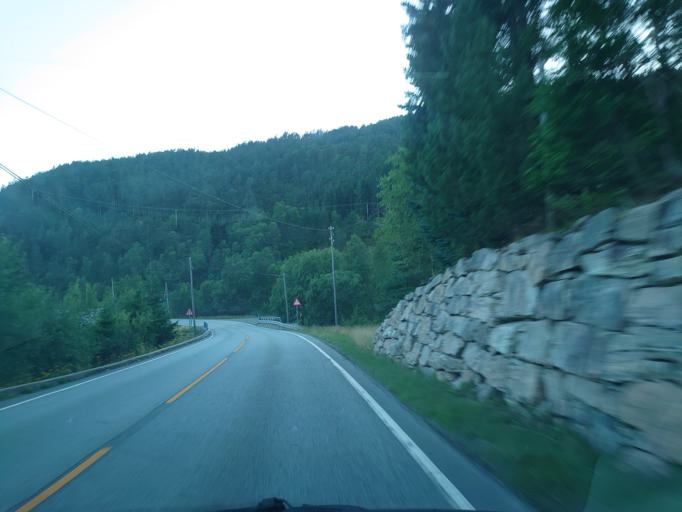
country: NO
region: Hordaland
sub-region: Modalen
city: Mo
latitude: 60.7171
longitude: 5.6329
